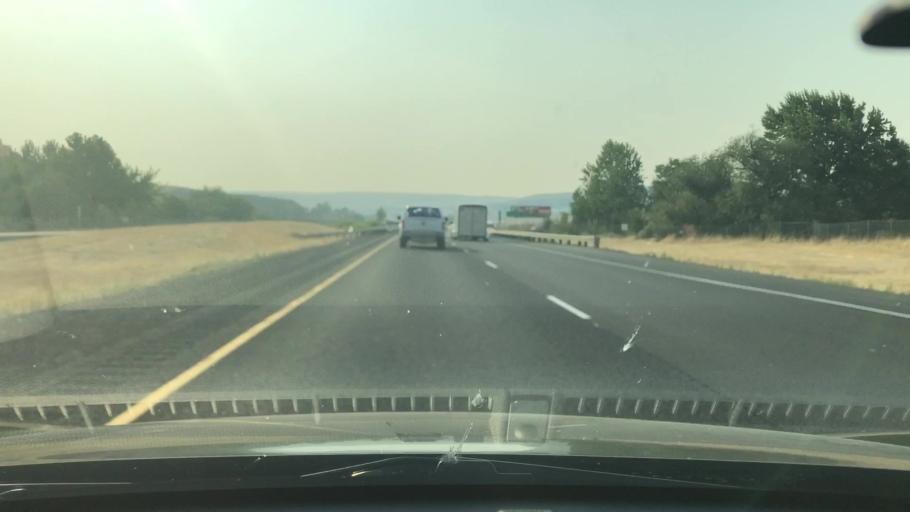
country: US
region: Oregon
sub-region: Umatilla County
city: Pendleton
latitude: 45.6662
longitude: -118.8147
